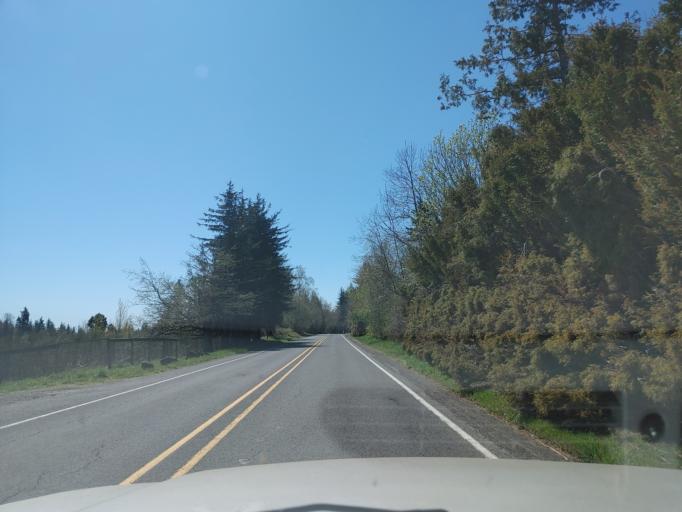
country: US
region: Washington
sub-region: Clark County
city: Washougal
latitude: 45.5322
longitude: -122.2691
